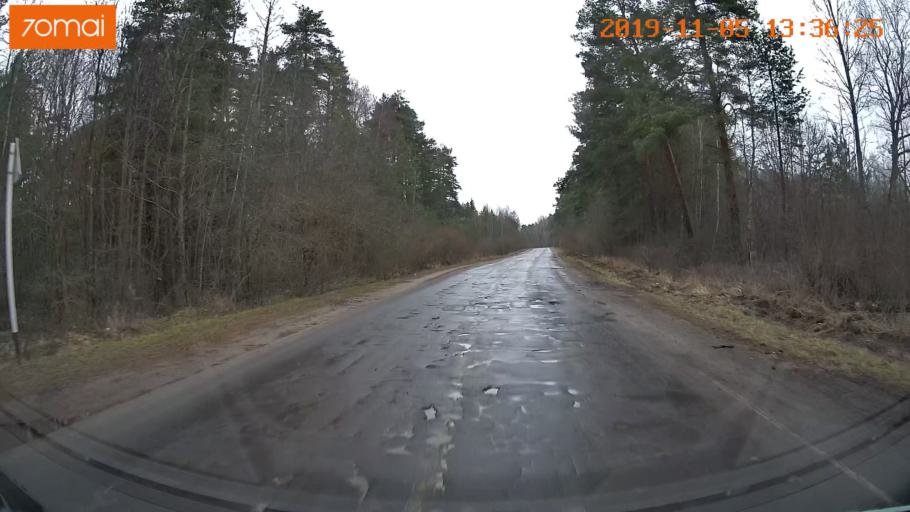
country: RU
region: Ivanovo
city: Shuya
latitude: 56.9145
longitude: 41.3824
